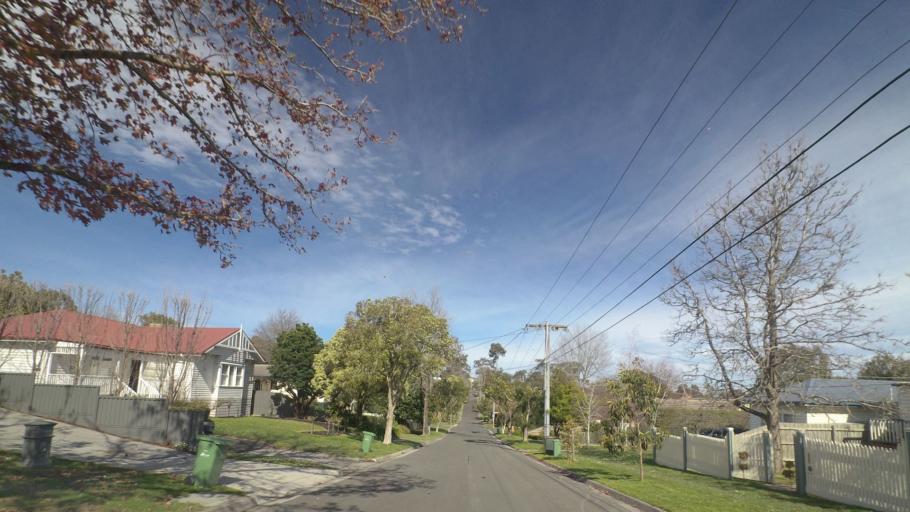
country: AU
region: Victoria
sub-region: Maroondah
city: Ringwood East
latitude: -37.8210
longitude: 145.2439
